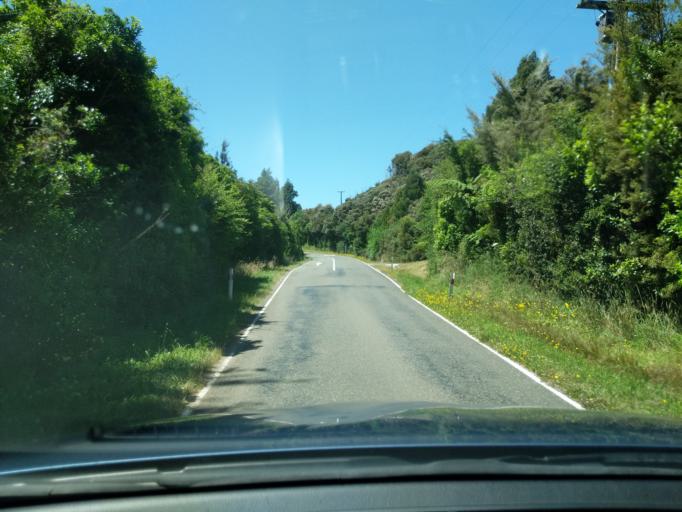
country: NZ
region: Tasman
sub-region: Tasman District
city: Takaka
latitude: -40.7277
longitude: 172.5849
